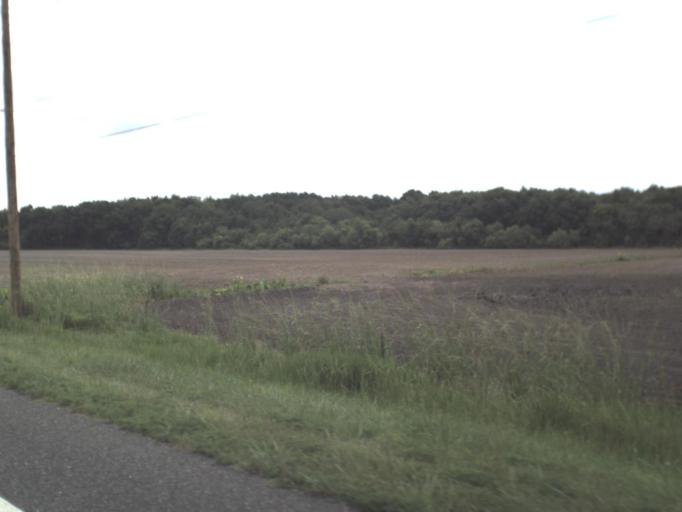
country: US
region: Florida
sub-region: Nassau County
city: Callahan
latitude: 30.6232
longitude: -81.8470
